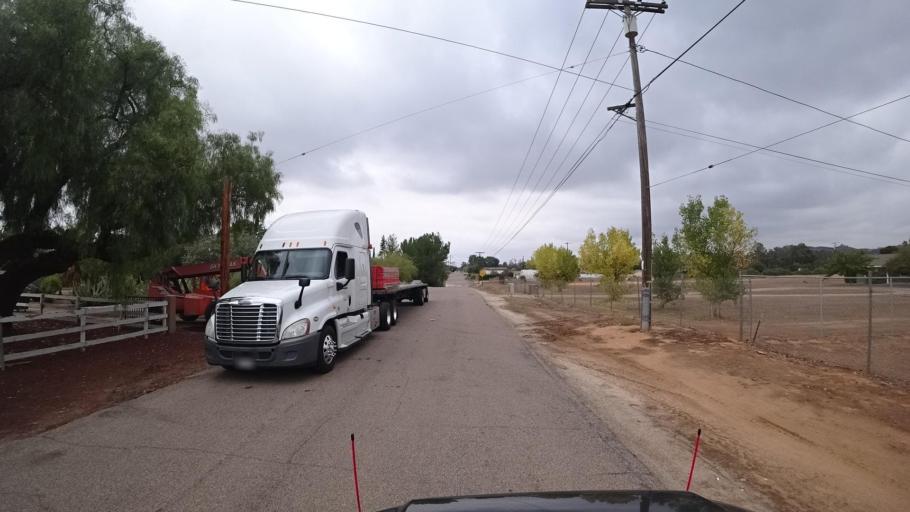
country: US
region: California
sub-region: San Diego County
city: Ramona
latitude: 33.0228
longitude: -116.8578
